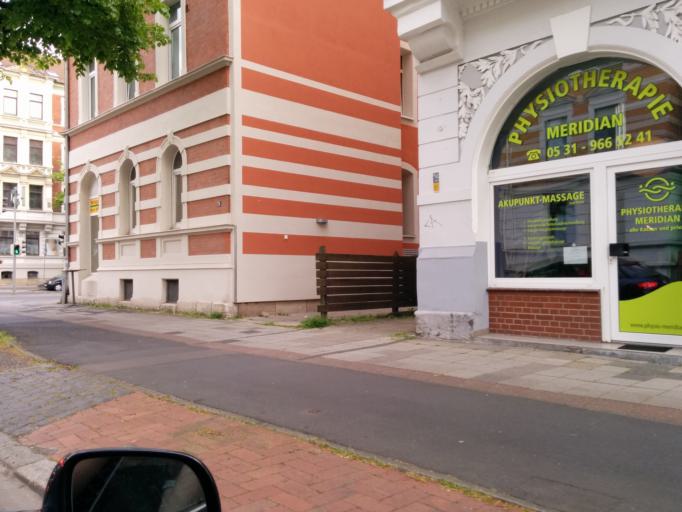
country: DE
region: Lower Saxony
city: Braunschweig
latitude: 52.2602
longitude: 10.5422
